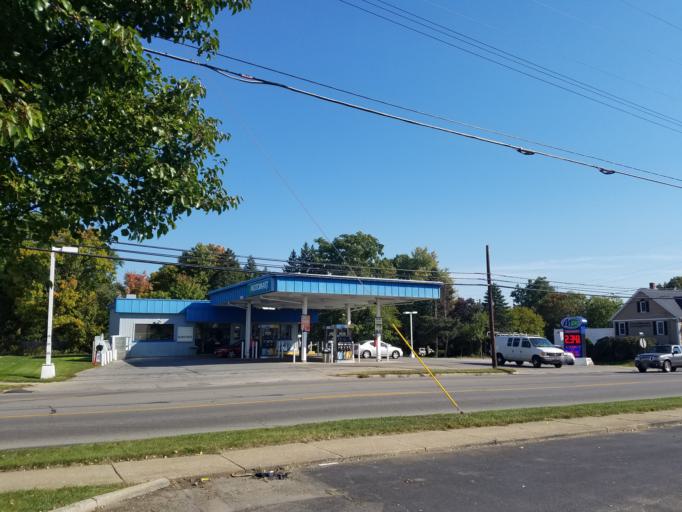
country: US
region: Ohio
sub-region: Ashland County
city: Ashland
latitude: 40.8666
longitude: -82.3027
